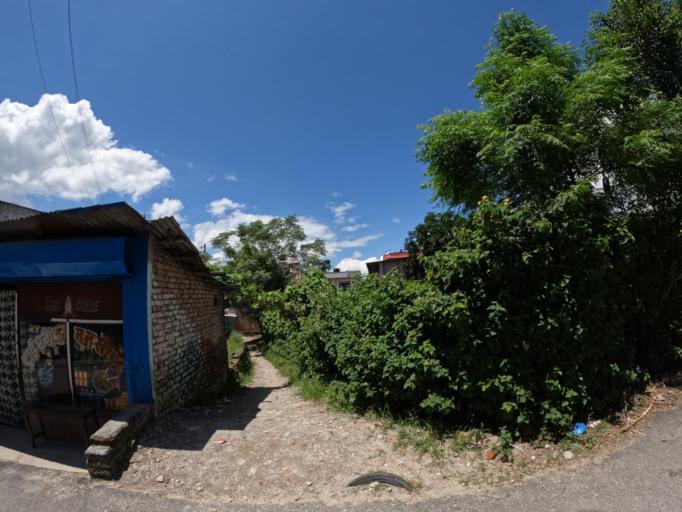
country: NP
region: Central Region
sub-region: Bagmati Zone
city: Kathmandu
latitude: 27.7466
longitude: 85.3270
